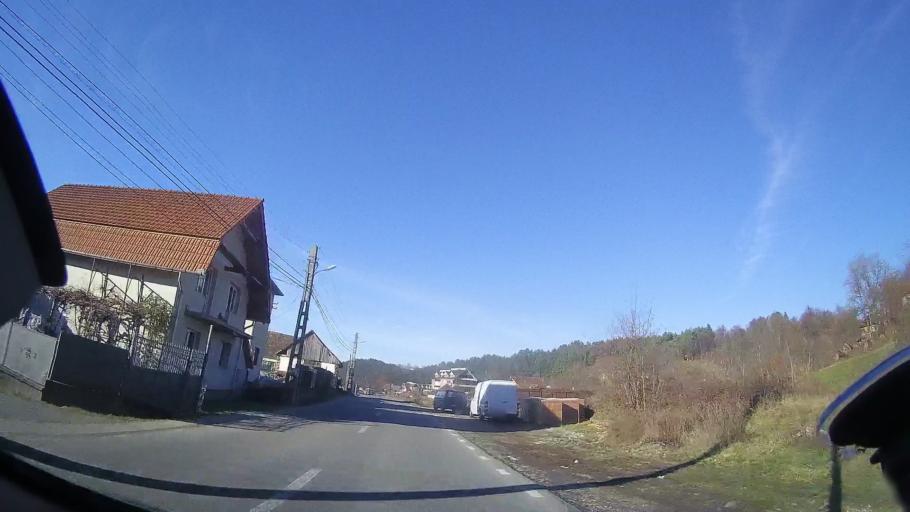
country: RO
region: Bihor
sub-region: Comuna Bratca
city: Bratca
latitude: 46.9269
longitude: 22.6084
